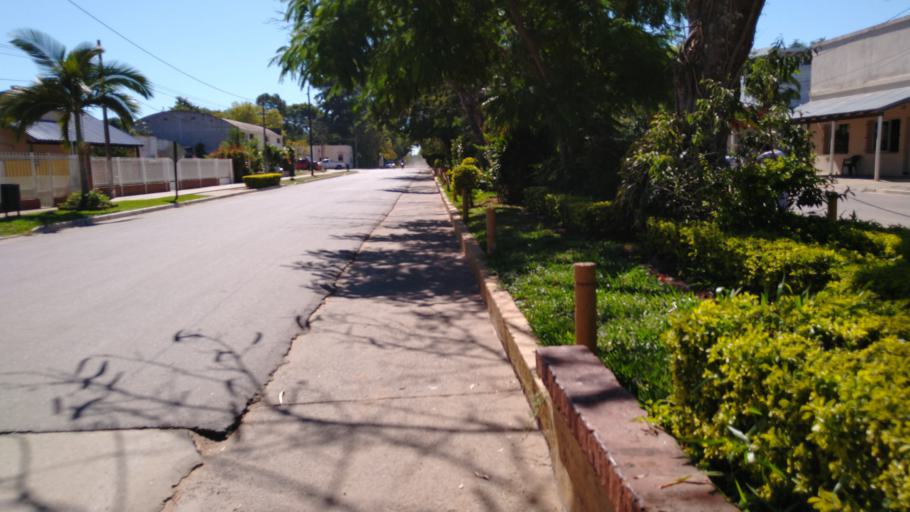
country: AR
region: Corrientes
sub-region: Departamento de San Miguel
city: San Miguel
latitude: -27.9955
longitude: -57.5925
